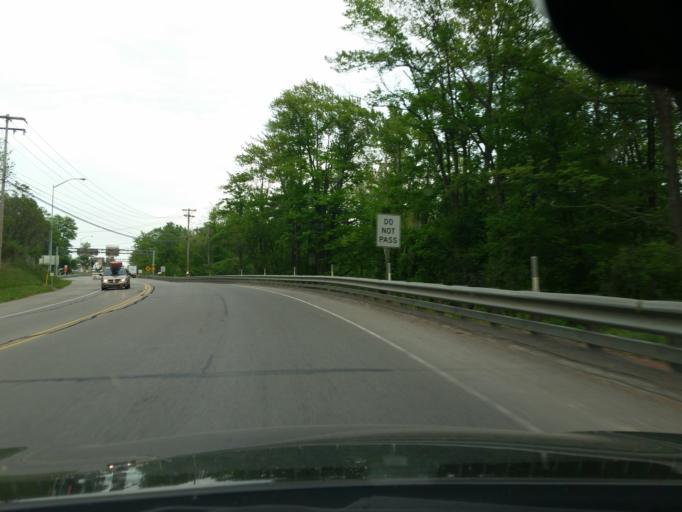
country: US
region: Pennsylvania
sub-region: Elk County
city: Ridgway
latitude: 41.4126
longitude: -78.7144
